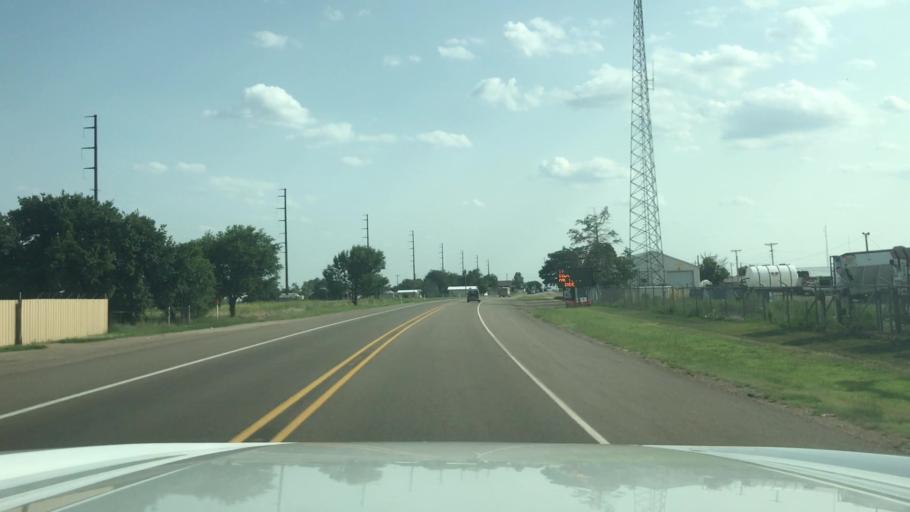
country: US
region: Texas
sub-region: Hartley County
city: Channing
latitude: 35.6894
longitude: -102.3283
